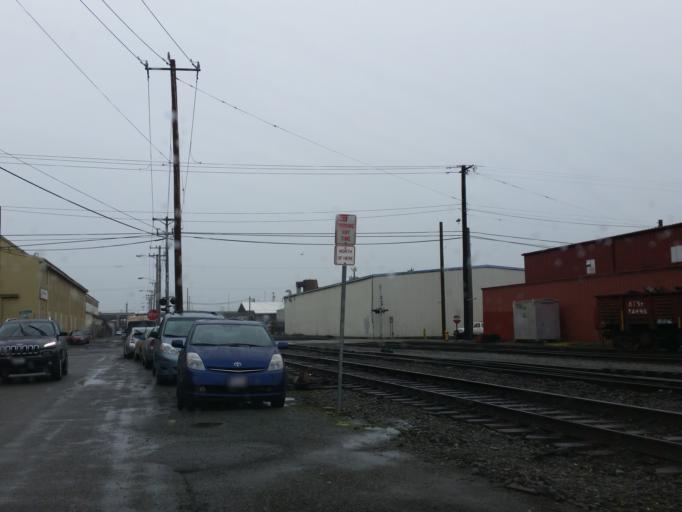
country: US
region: Washington
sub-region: King County
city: Seattle
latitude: 47.5750
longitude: -122.3368
